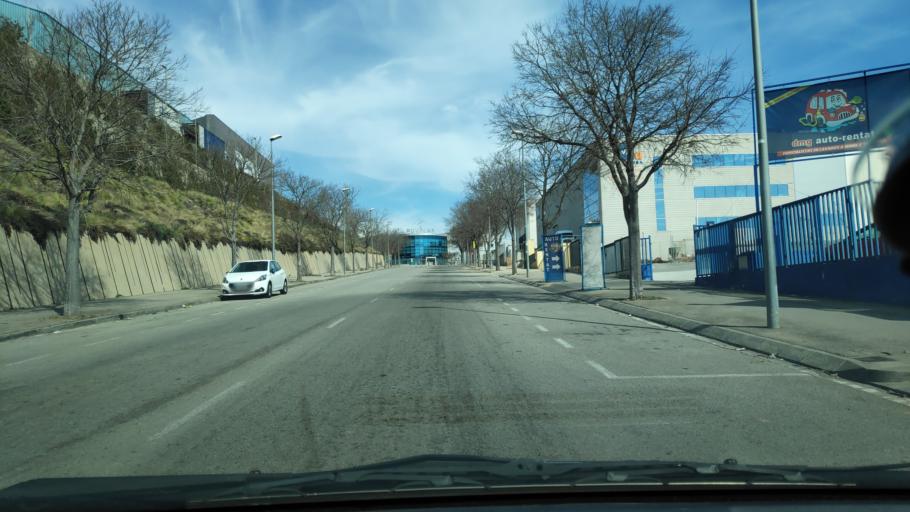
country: ES
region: Catalonia
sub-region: Provincia de Barcelona
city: Rubi
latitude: 41.5073
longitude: 2.0370
